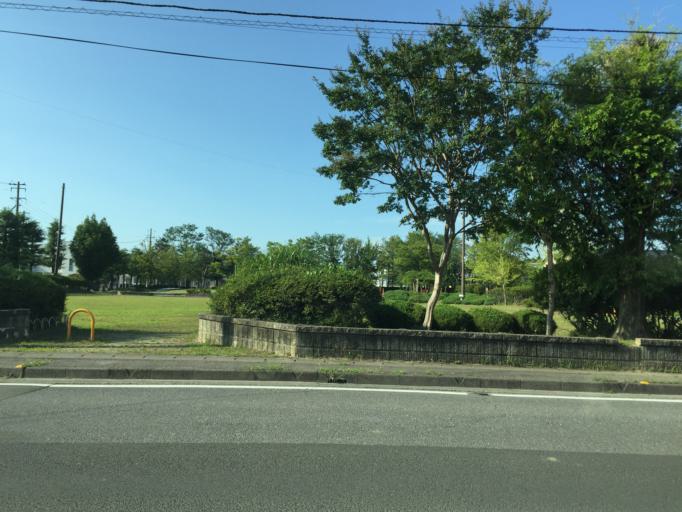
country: JP
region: Miyagi
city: Marumori
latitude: 37.8038
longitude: 140.9142
